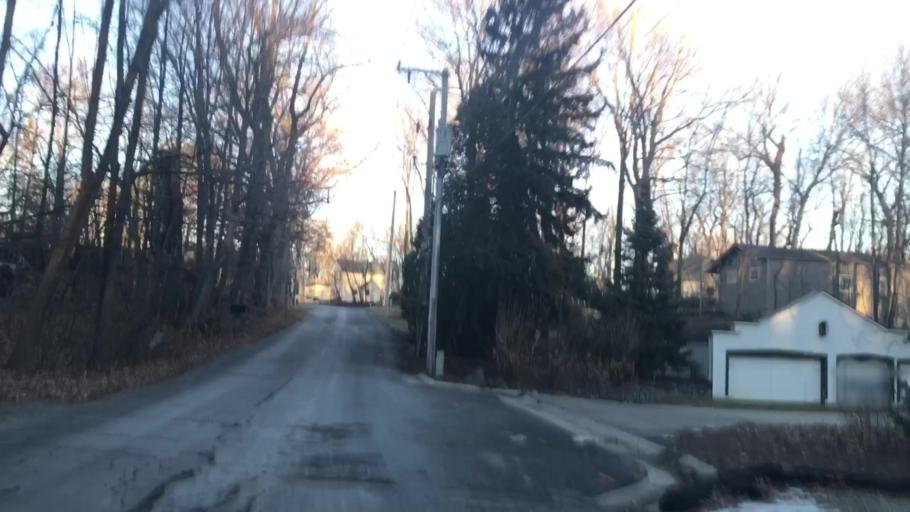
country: US
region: Wisconsin
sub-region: Washington County
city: Slinger
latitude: 43.3804
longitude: -88.2698
